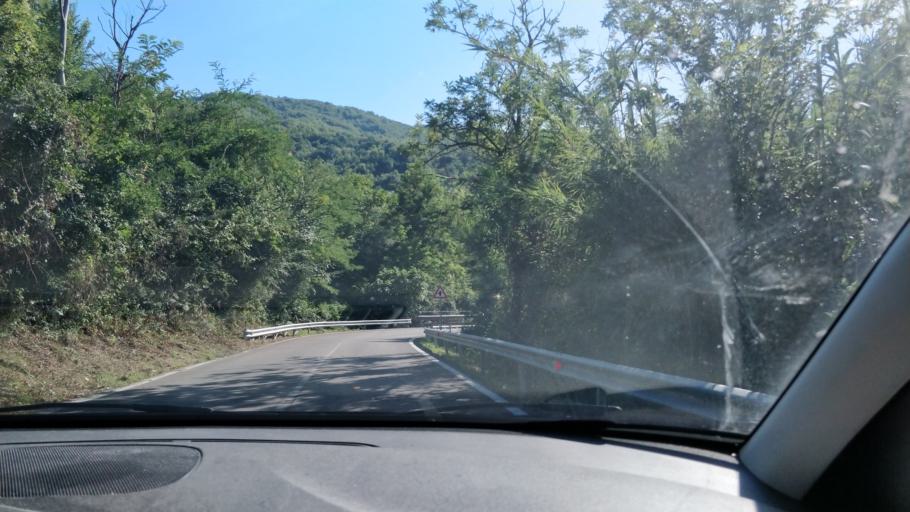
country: IT
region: Abruzzo
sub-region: Provincia di Pescara
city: Serramonacesca
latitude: 42.2473
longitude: 14.0896
